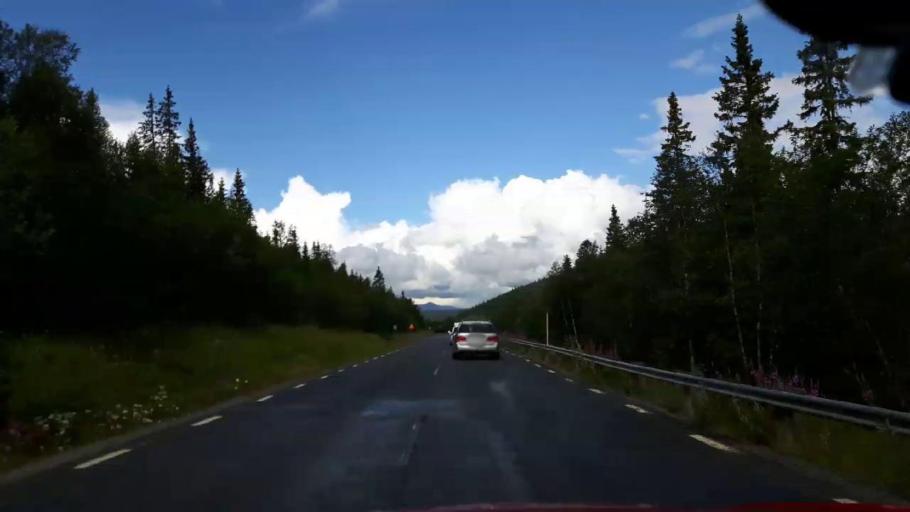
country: SE
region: Vaesterbotten
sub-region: Vilhelmina Kommun
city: Sjoberg
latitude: 65.0284
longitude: 15.1438
